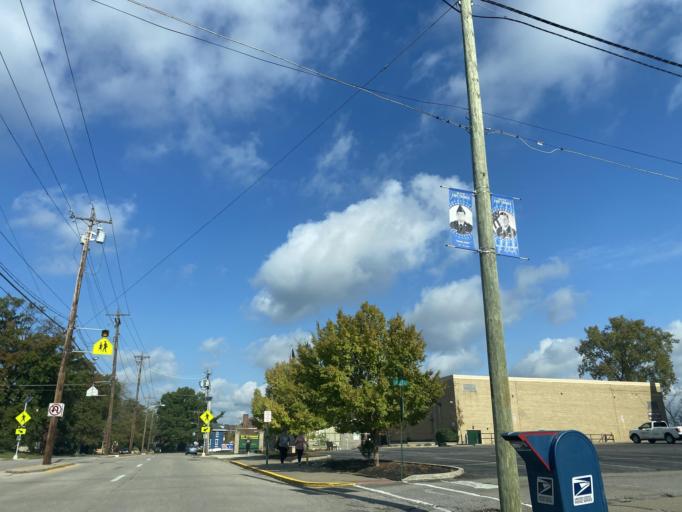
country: US
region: Kentucky
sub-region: Campbell County
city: Fort Thomas
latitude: 39.0726
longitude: -84.4463
